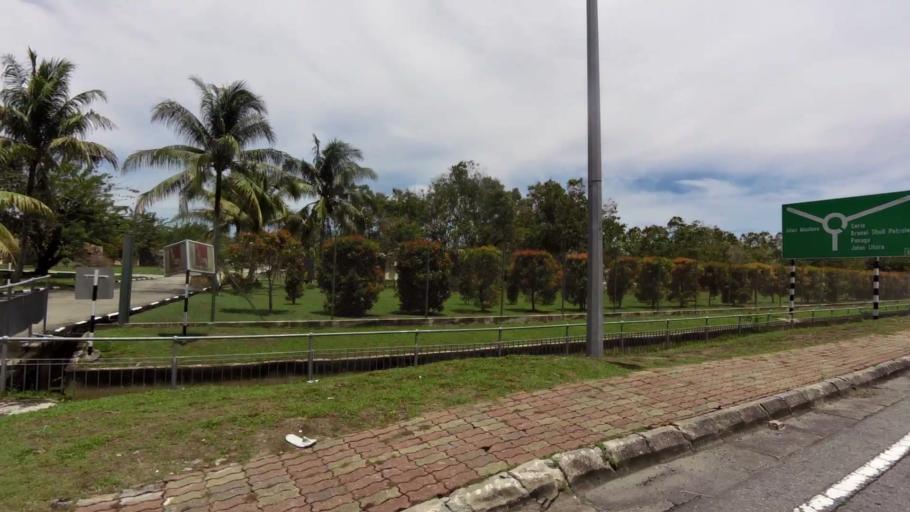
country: BN
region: Belait
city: Kuala Belait
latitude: 4.5933
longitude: 114.2560
